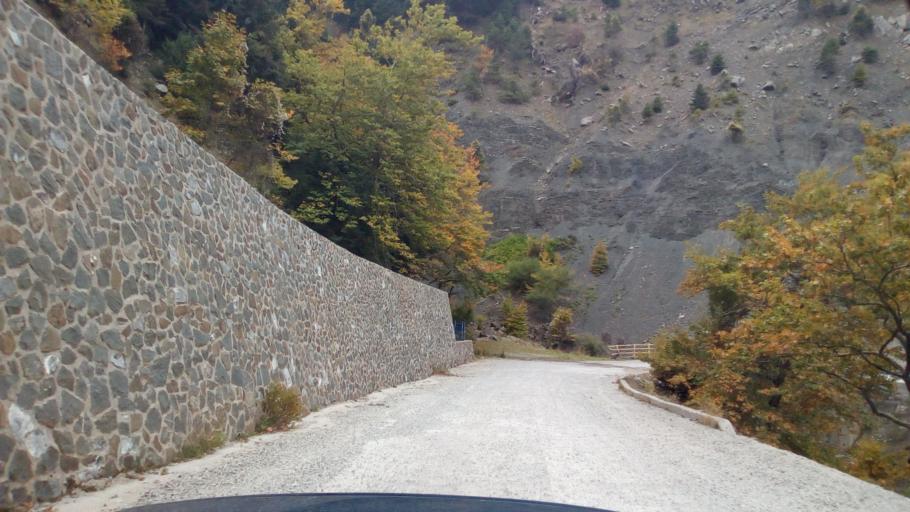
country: GR
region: Central Greece
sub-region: Nomos Fokidos
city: Lidoriki
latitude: 38.4746
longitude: 22.0723
